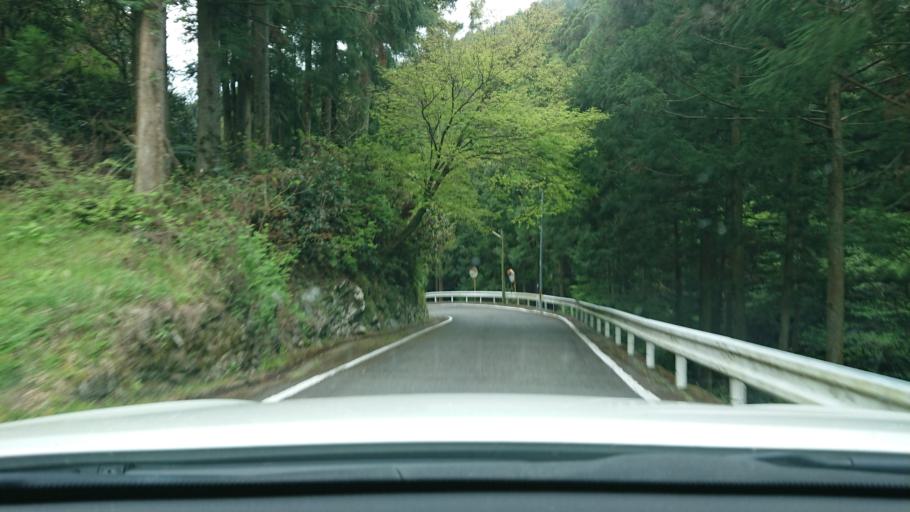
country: JP
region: Tokushima
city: Ishii
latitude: 33.8874
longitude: 134.3967
